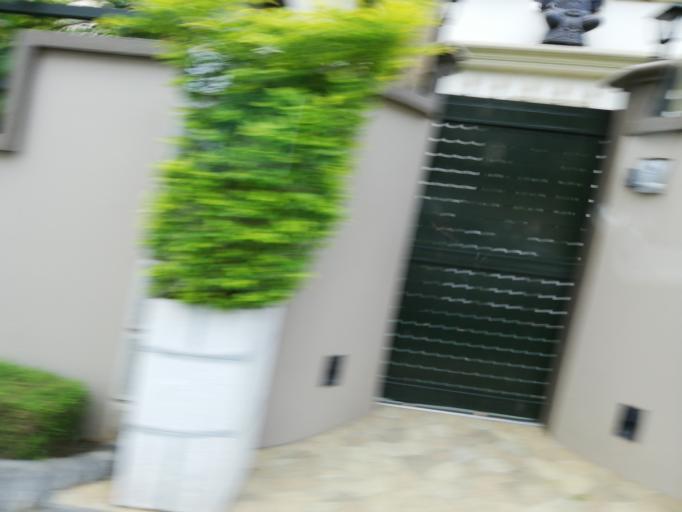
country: MU
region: Black River
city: Gros Cailloux
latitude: -20.2347
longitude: 57.4542
